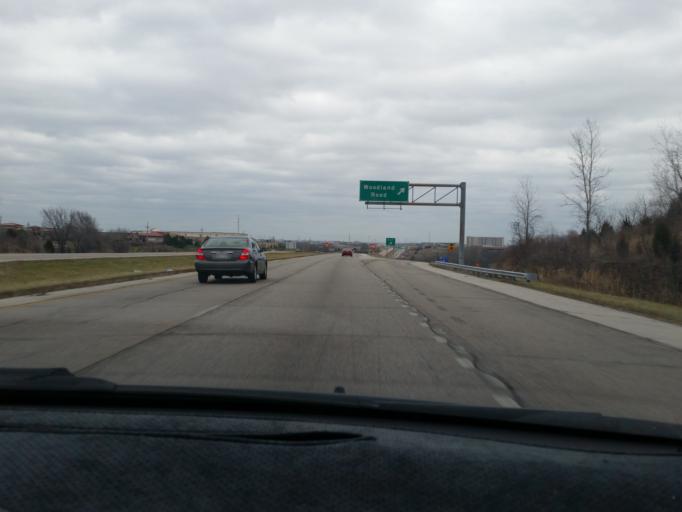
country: US
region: Kansas
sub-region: Johnson County
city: Olathe
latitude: 38.9417
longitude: -94.8205
